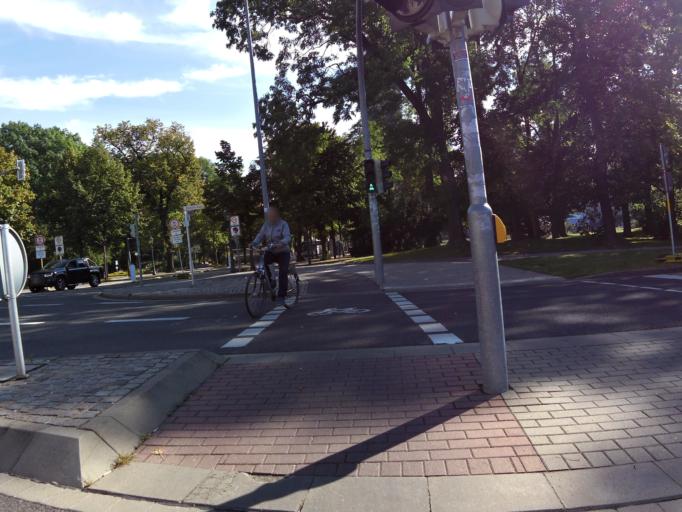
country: DE
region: Saxony-Anhalt
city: Wittenburg
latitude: 51.8668
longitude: 12.6353
